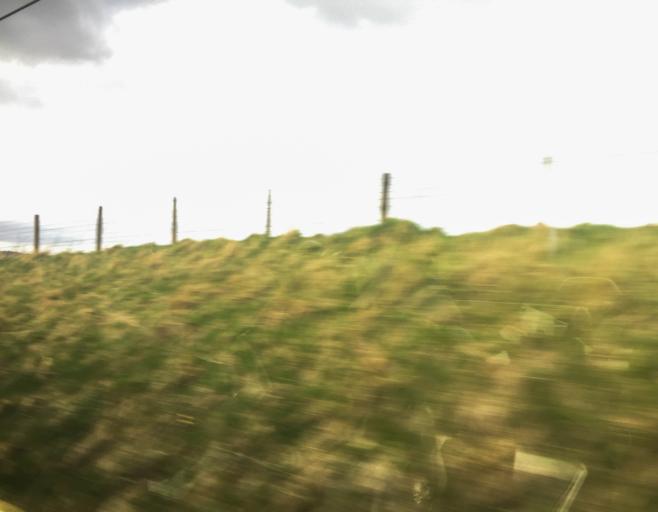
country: GB
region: Scotland
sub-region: South Lanarkshire
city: Carnwath
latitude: 55.6770
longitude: -3.6479
